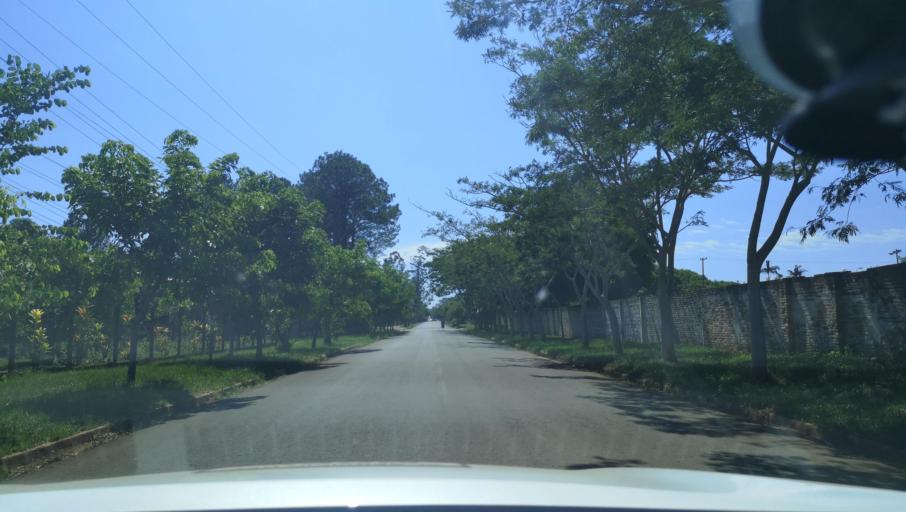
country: PY
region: Itapua
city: Carmen del Parana
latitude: -27.1595
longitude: -56.2436
